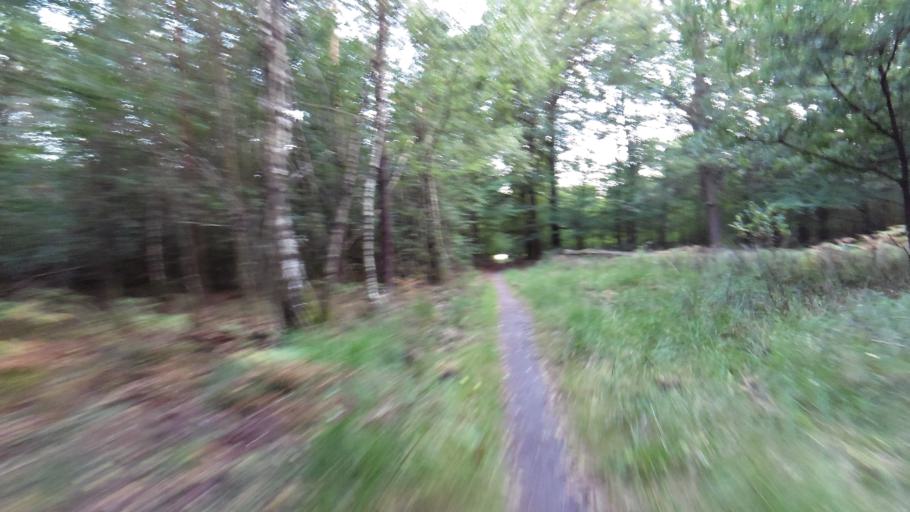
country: NL
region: Gelderland
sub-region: Gemeente Apeldoorn
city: Uddel
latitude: 52.2463
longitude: 5.8656
